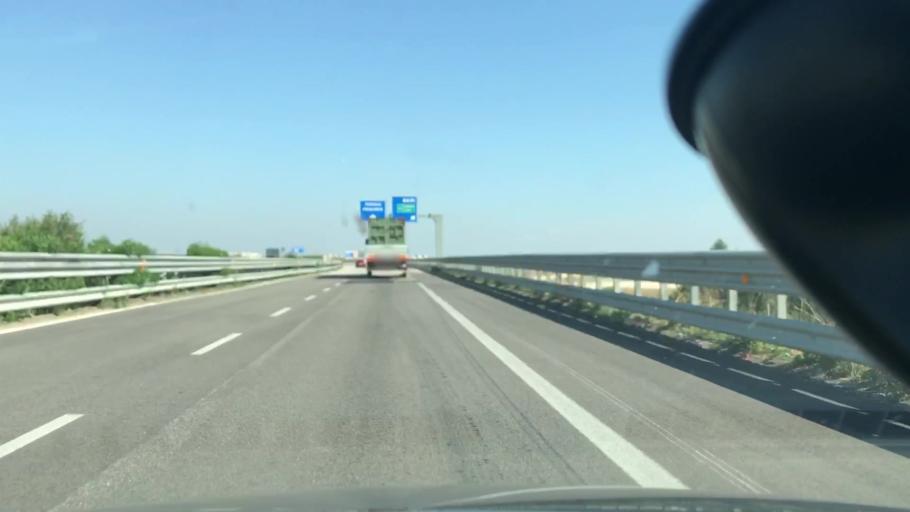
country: IT
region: Apulia
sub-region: Provincia di Foggia
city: Foggia
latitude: 41.4215
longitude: 15.5590
